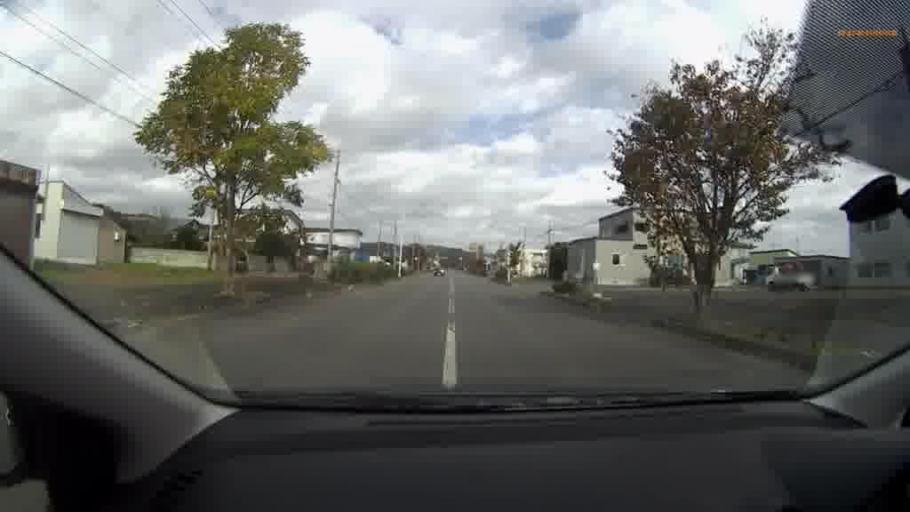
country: JP
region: Hokkaido
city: Kushiro
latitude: 42.9786
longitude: 144.1282
